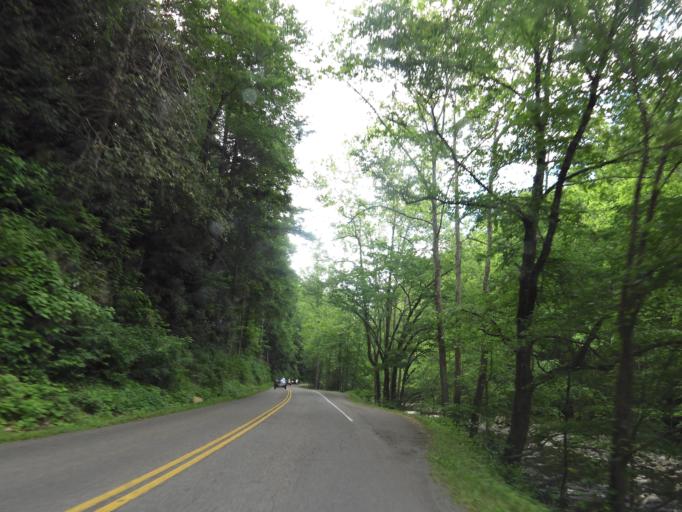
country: US
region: Tennessee
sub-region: Sevier County
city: Gatlinburg
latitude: 35.6640
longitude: -83.6343
